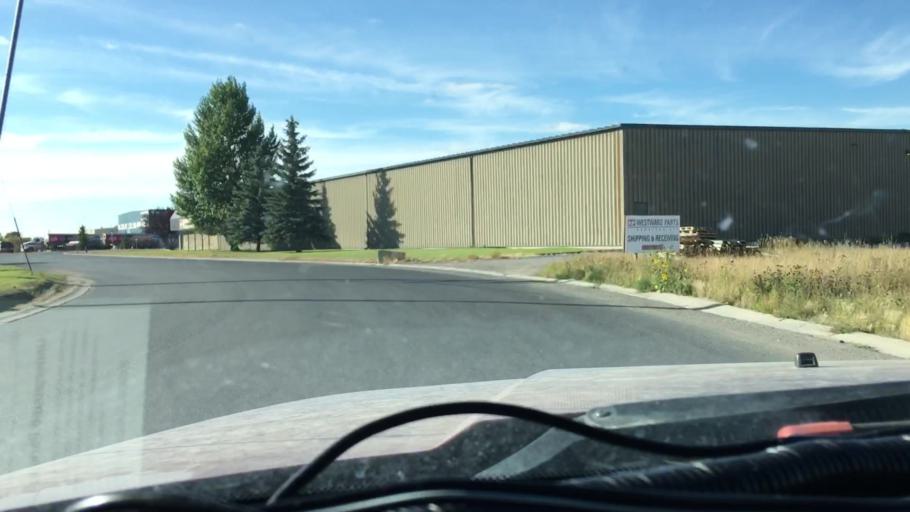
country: CA
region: Saskatchewan
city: Regina
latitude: 50.4781
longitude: -104.5618
